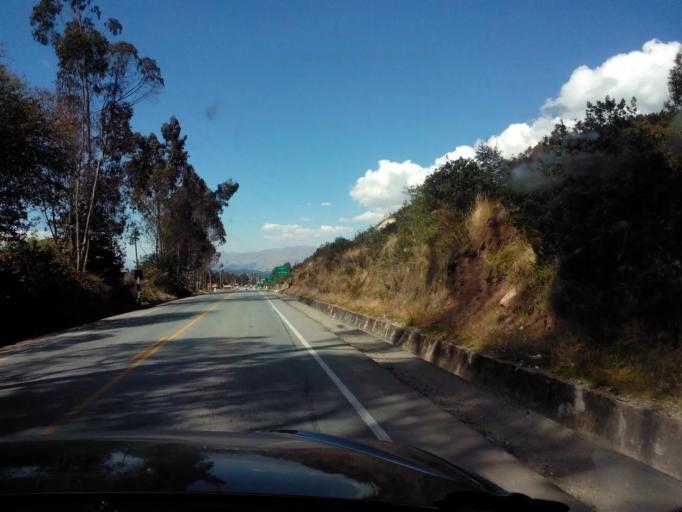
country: PE
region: Cusco
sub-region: Provincia de Anta
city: Ancahuasi
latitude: -13.4403
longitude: -72.3571
